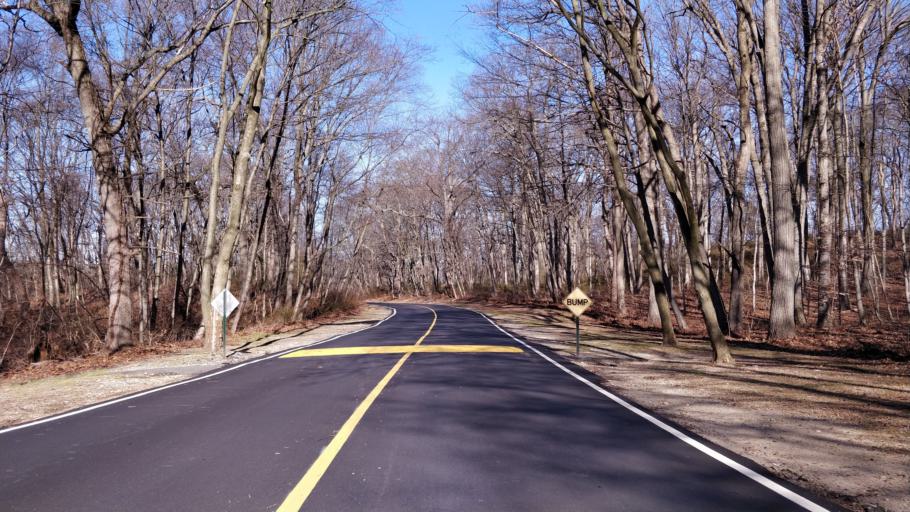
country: US
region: New York
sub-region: Nassau County
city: Greenvale
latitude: 40.8100
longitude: -73.6102
